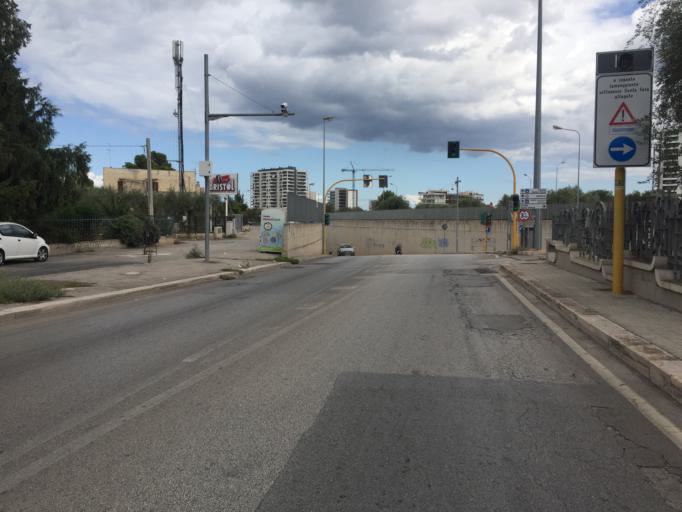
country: IT
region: Apulia
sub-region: Provincia di Bari
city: Bari
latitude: 41.1013
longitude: 16.8483
